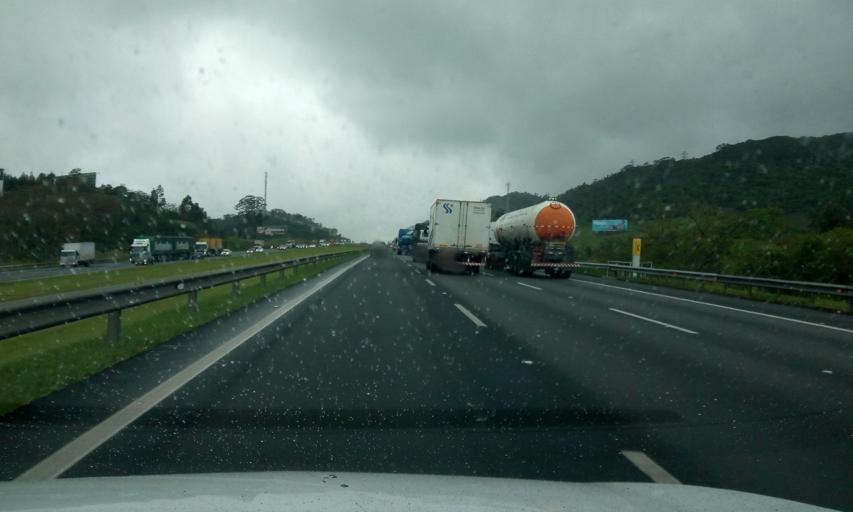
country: BR
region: Sao Paulo
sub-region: Jundiai
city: Jundiai
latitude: -23.2174
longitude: -46.9153
